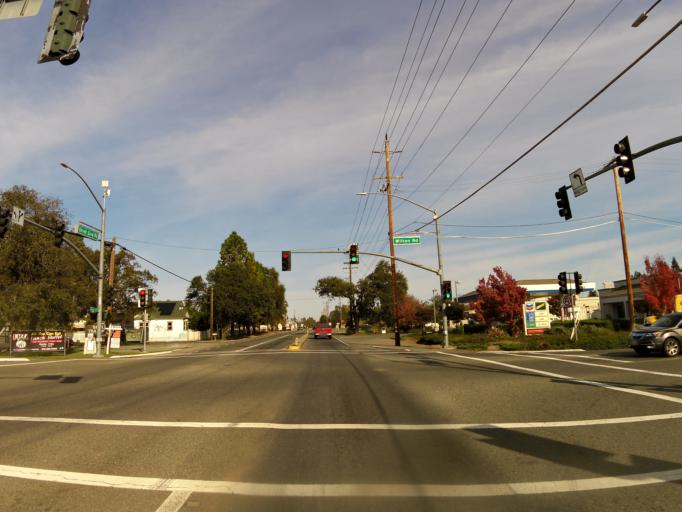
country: US
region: California
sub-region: Sacramento County
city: Wilton
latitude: 38.4308
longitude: -121.3009
